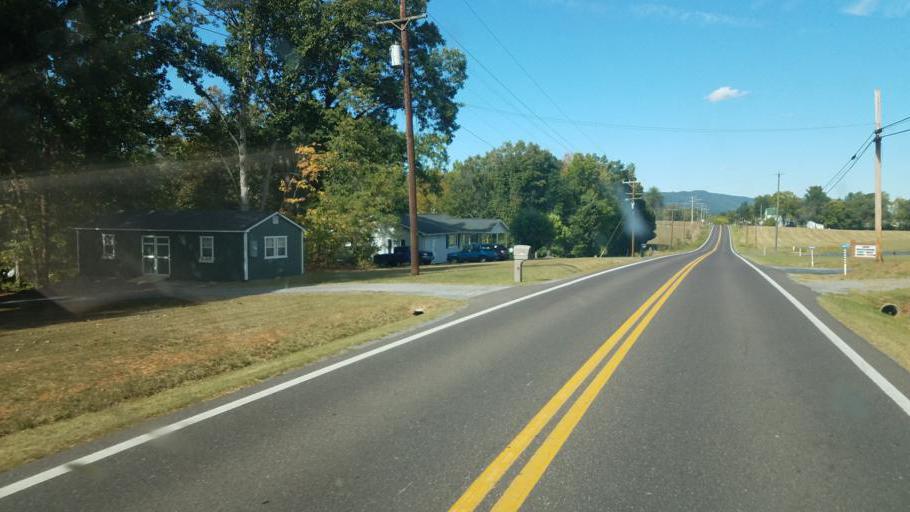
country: US
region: Virginia
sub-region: Page County
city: Luray
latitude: 38.7530
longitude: -78.4015
